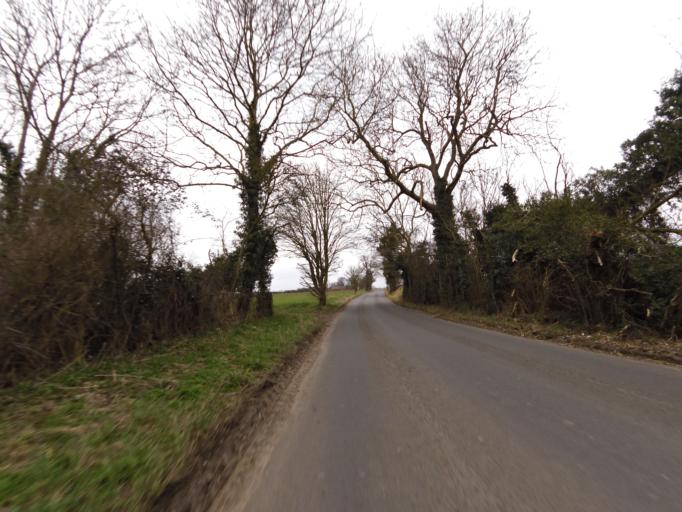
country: GB
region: England
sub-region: Suffolk
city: Ipswich
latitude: 52.1221
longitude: 1.1599
